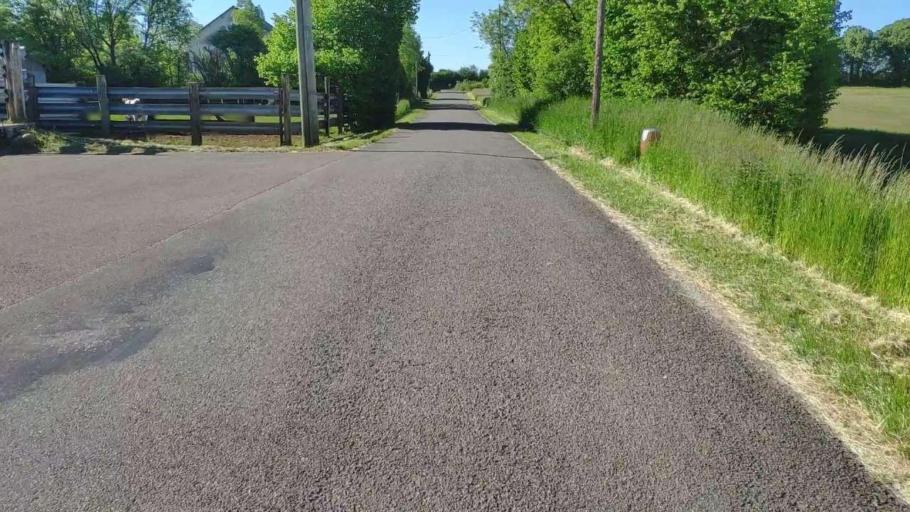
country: FR
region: Franche-Comte
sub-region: Departement du Jura
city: Perrigny
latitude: 46.6871
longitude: 5.6383
